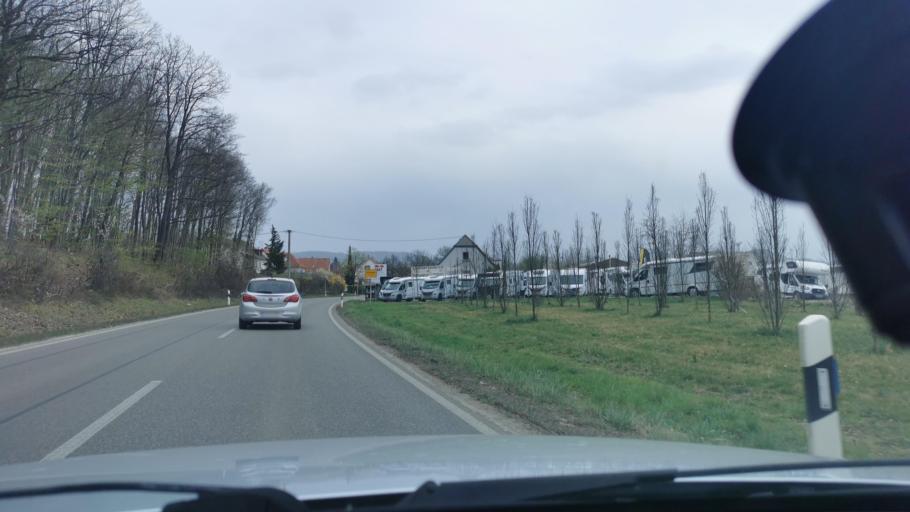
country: DE
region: Baden-Wuerttemberg
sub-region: Regierungsbezirk Stuttgart
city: Holzmaden
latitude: 48.6325
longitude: 9.5090
